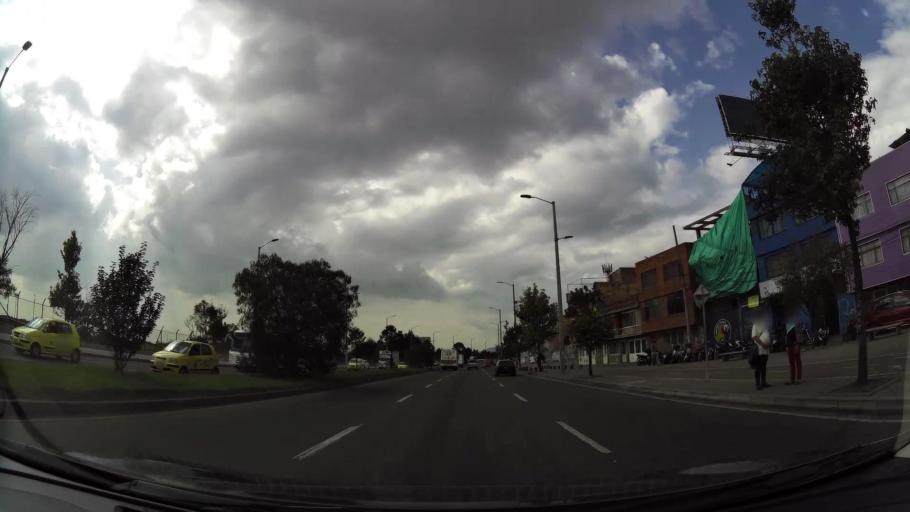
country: CO
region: Cundinamarca
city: Cota
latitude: 4.7232
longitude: -74.0980
